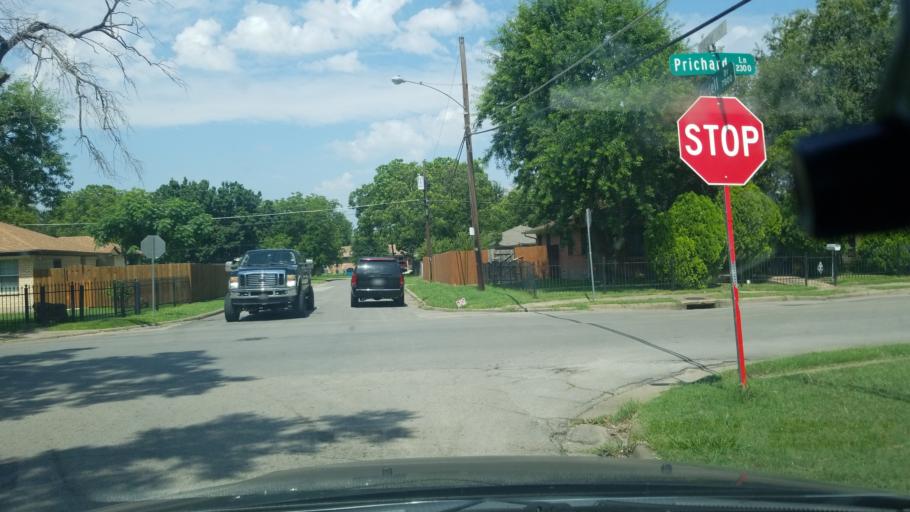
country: US
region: Texas
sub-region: Dallas County
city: Balch Springs
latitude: 32.7524
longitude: -96.6864
